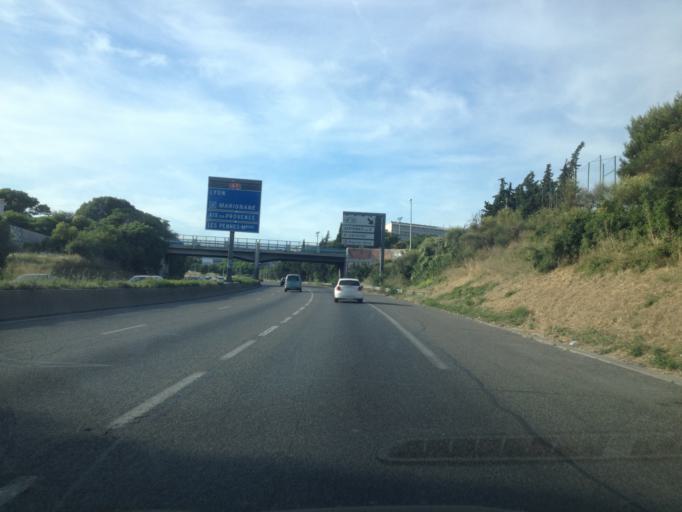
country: FR
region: Provence-Alpes-Cote d'Azur
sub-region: Departement des Bouches-du-Rhone
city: Marseille 15
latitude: 43.3719
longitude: 5.3613
